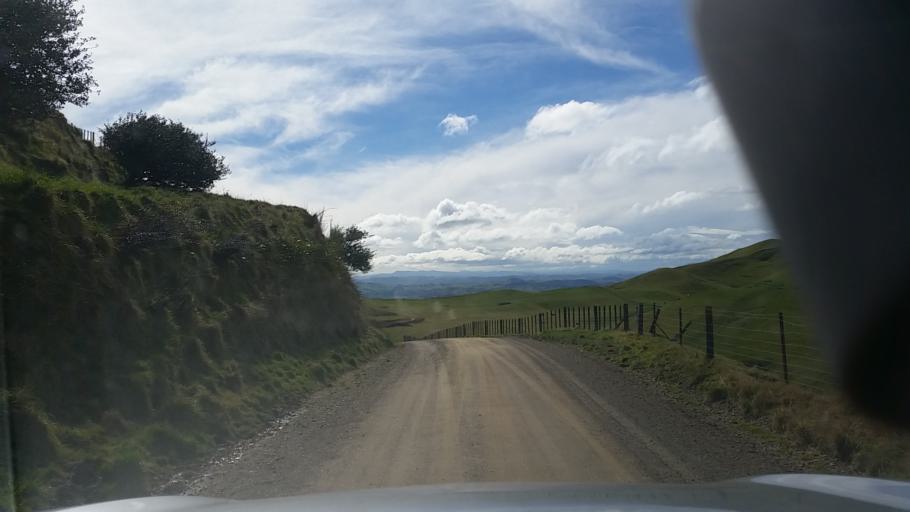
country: NZ
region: Hawke's Bay
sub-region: Napier City
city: Napier
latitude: -39.2012
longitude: 176.9515
